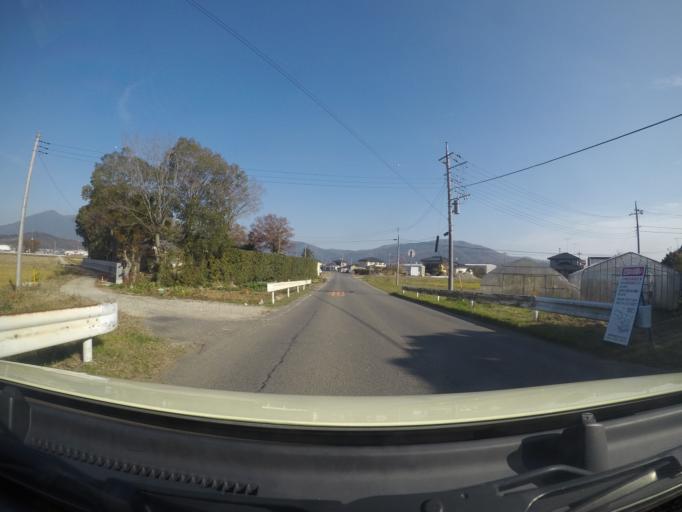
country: JP
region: Ibaraki
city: Tsukuba
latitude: 36.1627
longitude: 140.0863
